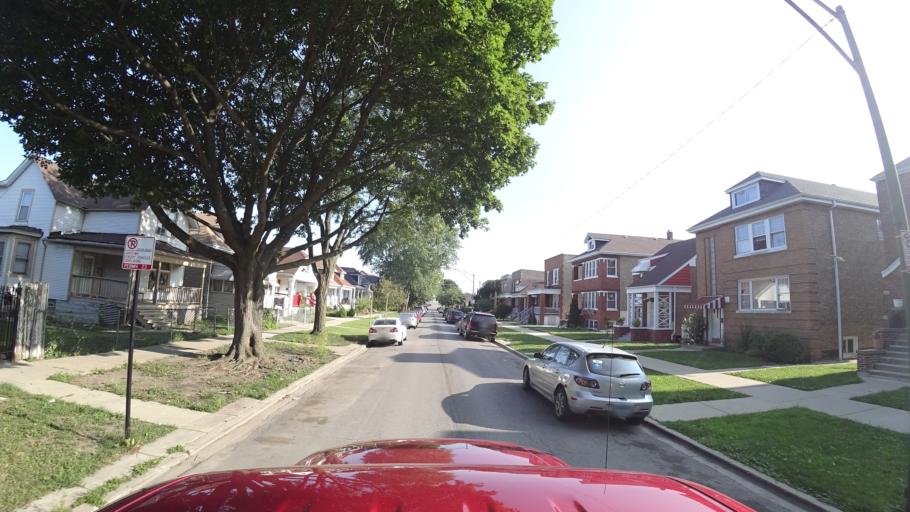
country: US
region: Illinois
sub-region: Cook County
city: Cicero
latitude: 41.7992
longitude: -87.7049
